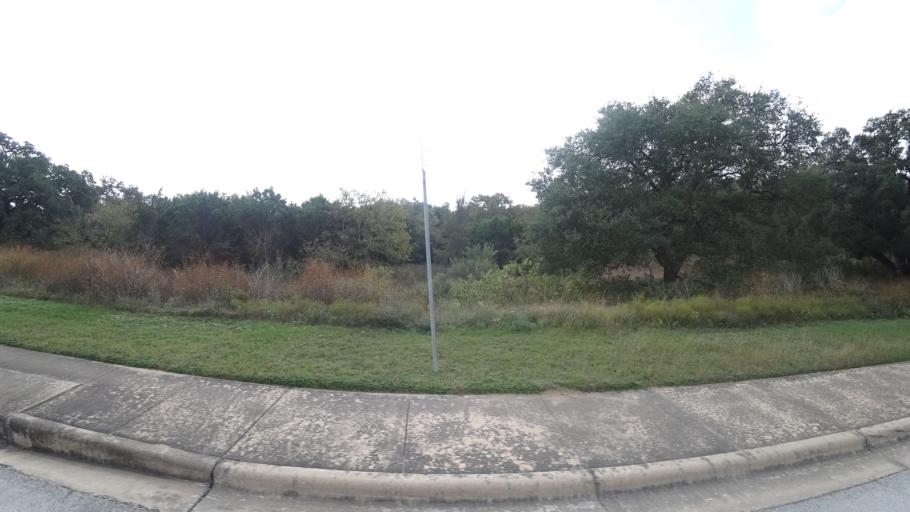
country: US
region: Texas
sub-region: Travis County
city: Barton Creek
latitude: 30.3043
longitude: -97.8892
